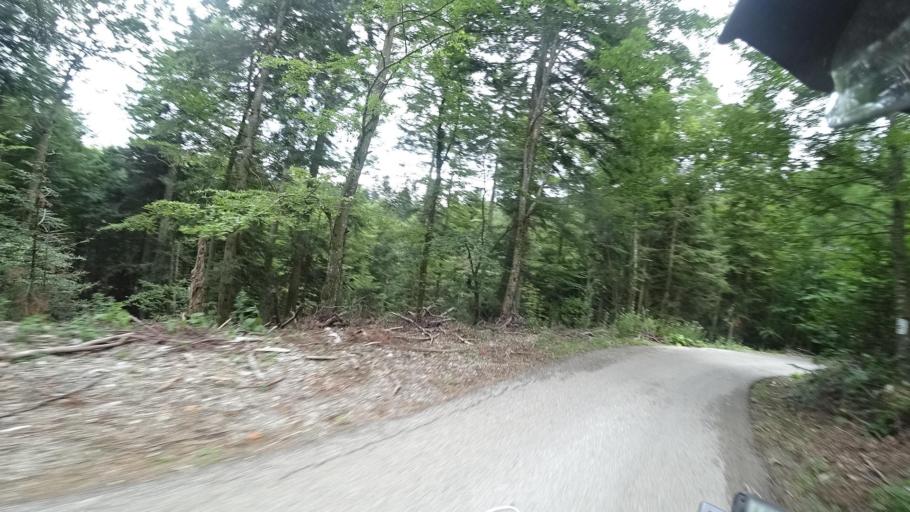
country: HR
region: Licko-Senjska
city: Senj
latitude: 45.1022
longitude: 14.9493
